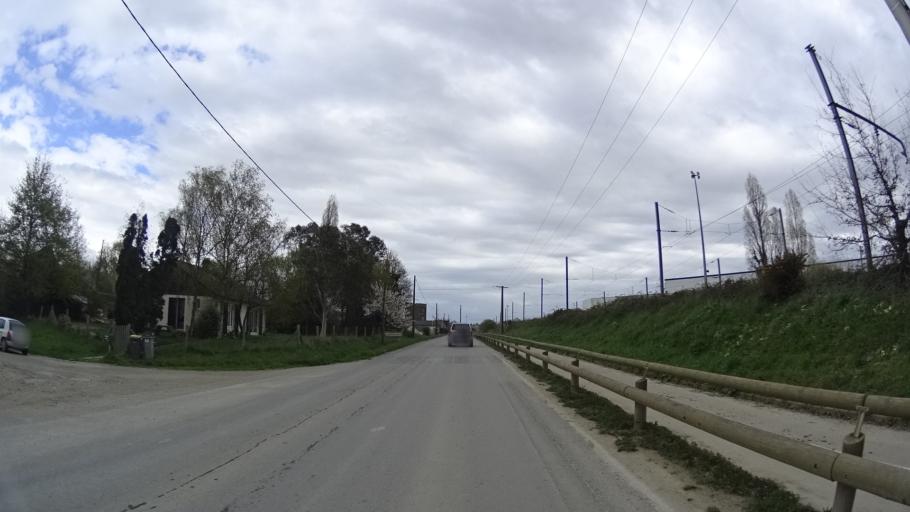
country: FR
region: Brittany
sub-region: Departement d'Ille-et-Vilaine
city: Saint-Gilles
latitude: 48.1225
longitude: -1.8272
